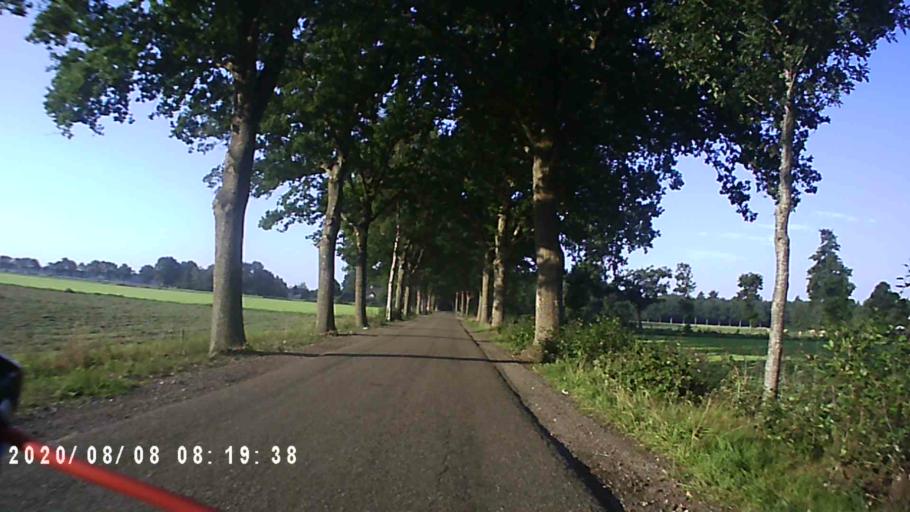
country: NL
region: Groningen
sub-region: Gemeente Leek
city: Leek
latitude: 53.0962
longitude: 6.3157
